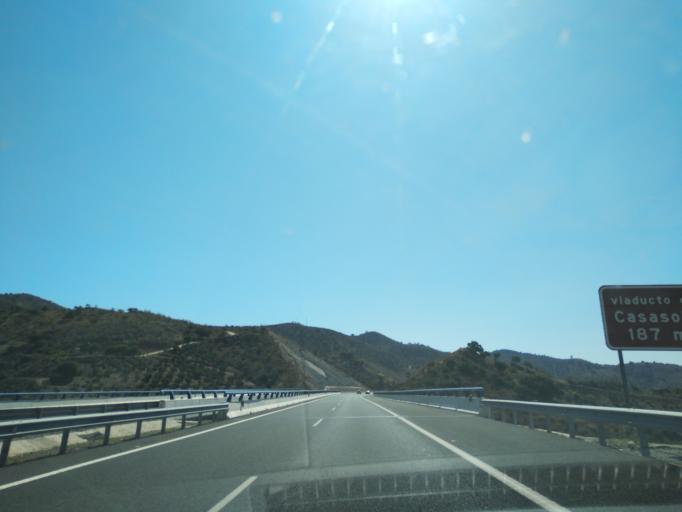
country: ES
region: Andalusia
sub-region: Provincia de Malaga
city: Almogia
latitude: 36.8031
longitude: -4.4697
